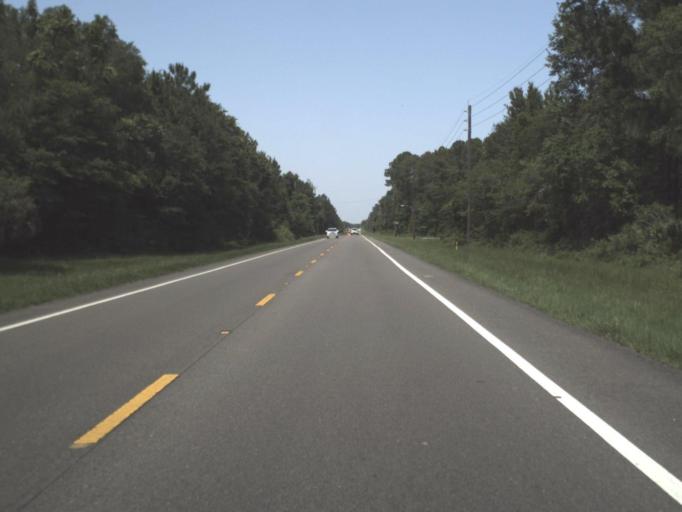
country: US
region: Florida
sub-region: Nassau County
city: Yulee
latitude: 30.5652
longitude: -81.6158
